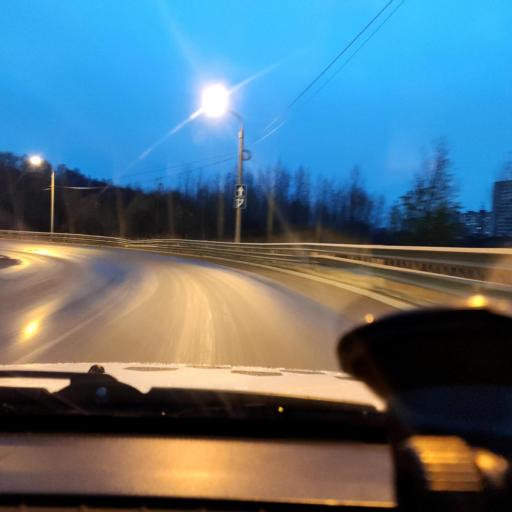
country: RU
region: Perm
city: Perm
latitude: 57.9616
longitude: 56.2066
